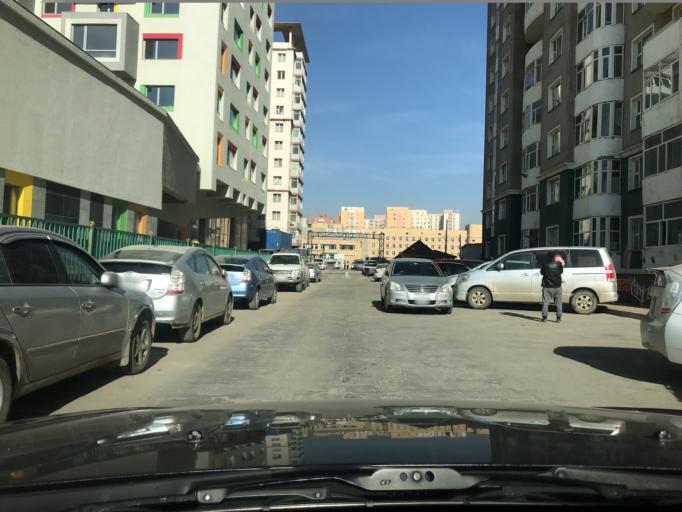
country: MN
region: Ulaanbaatar
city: Ulaanbaatar
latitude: 47.9114
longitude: 106.9468
